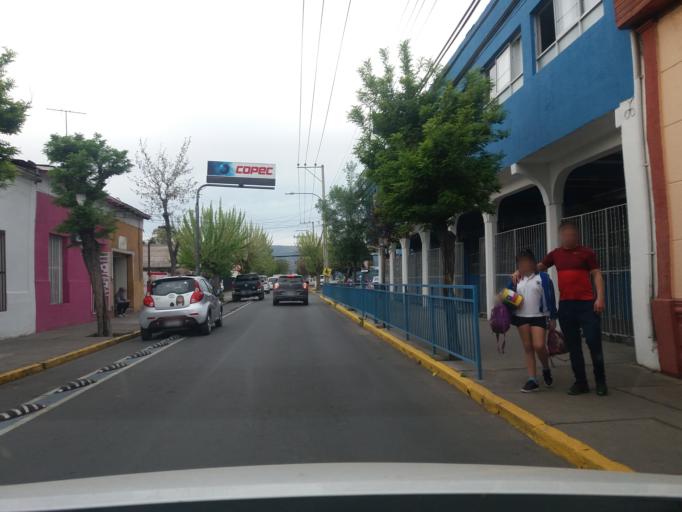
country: CL
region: Valparaiso
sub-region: Provincia de San Felipe
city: San Felipe
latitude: -32.7533
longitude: -70.7253
